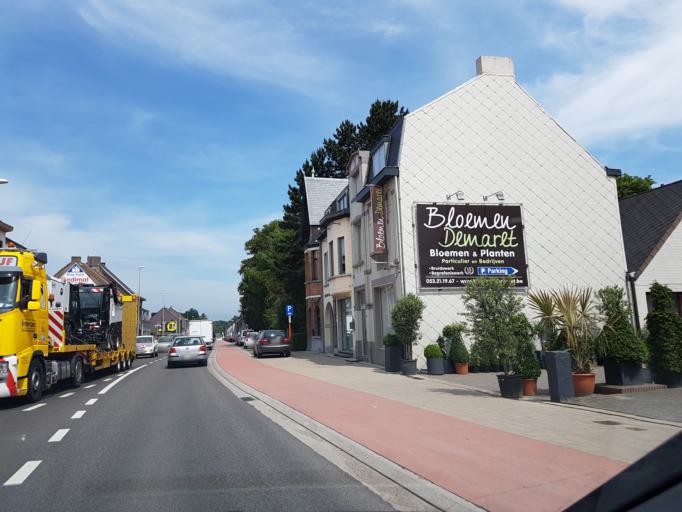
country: BE
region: Flanders
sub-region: Provincie Oost-Vlaanderen
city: Denderleeuw
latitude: 50.9213
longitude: 4.0697
